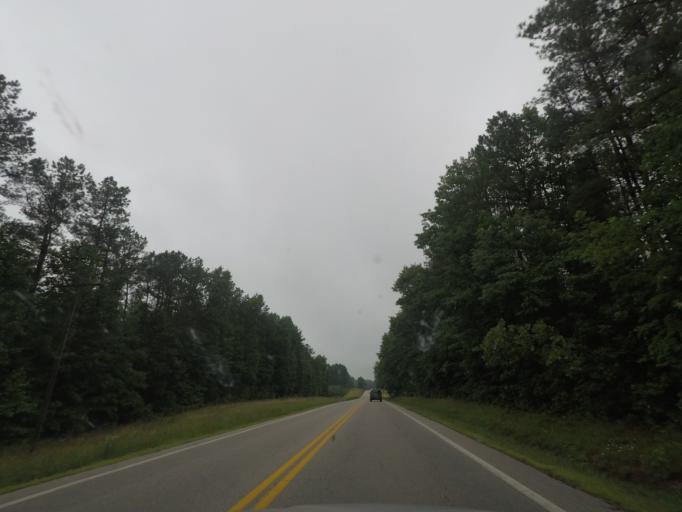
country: US
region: Virginia
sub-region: Prince Edward County
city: Hampden Sydney
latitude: 37.0893
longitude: -78.4746
